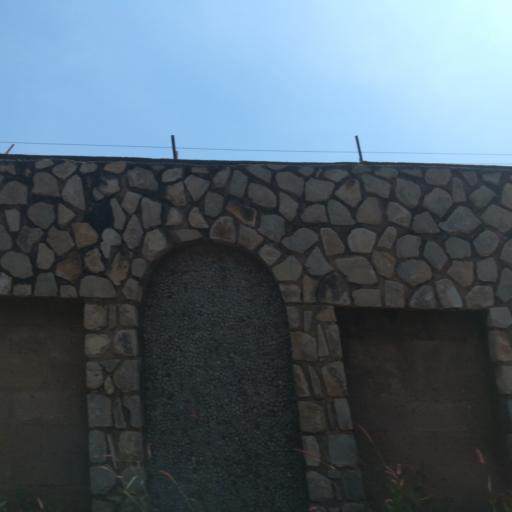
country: NG
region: Plateau
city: Bukuru
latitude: 9.8414
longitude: 8.9025
